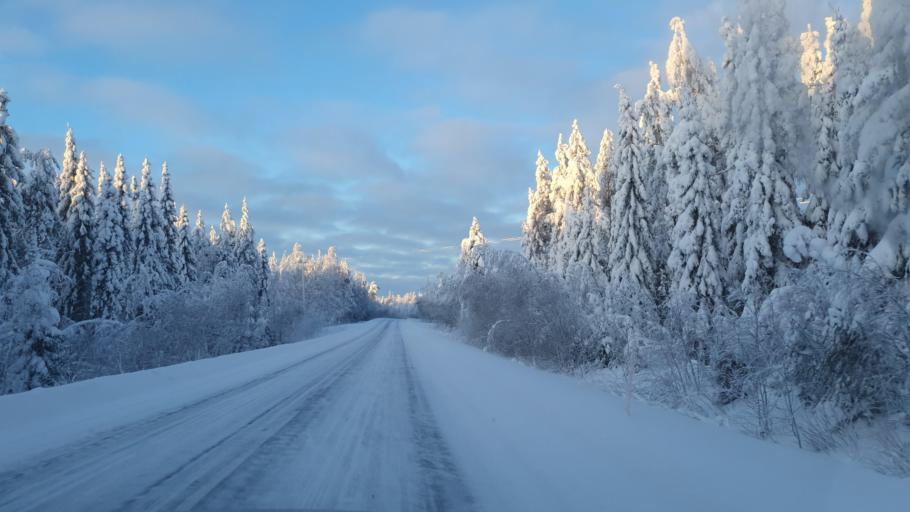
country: FI
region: Kainuu
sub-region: Kajaani
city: Vuokatti
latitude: 64.2750
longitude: 28.2320
